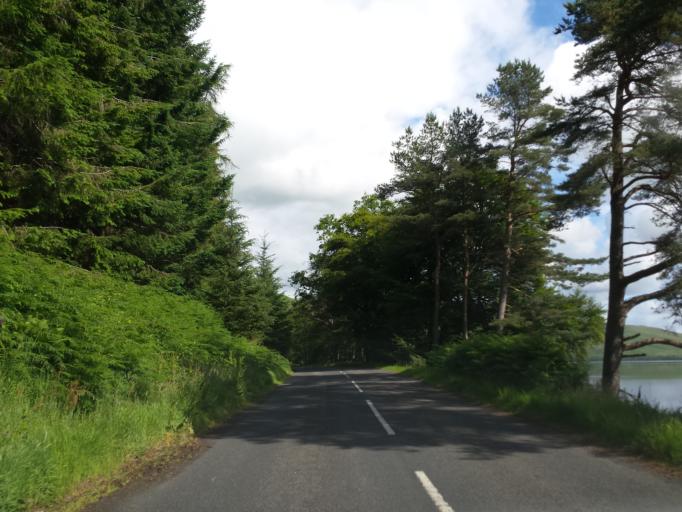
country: GB
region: Scotland
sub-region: The Scottish Borders
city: Peebles
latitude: 55.4745
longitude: -3.2073
